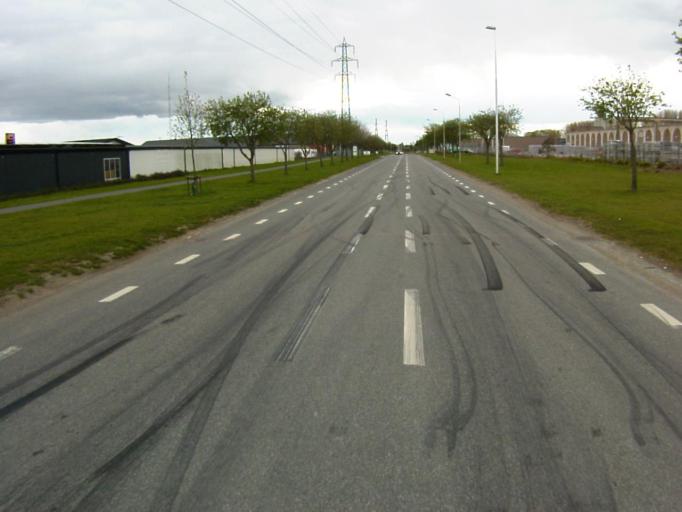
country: SE
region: Skane
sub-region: Kristianstads Kommun
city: Kristianstad
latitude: 56.0590
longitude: 14.1721
